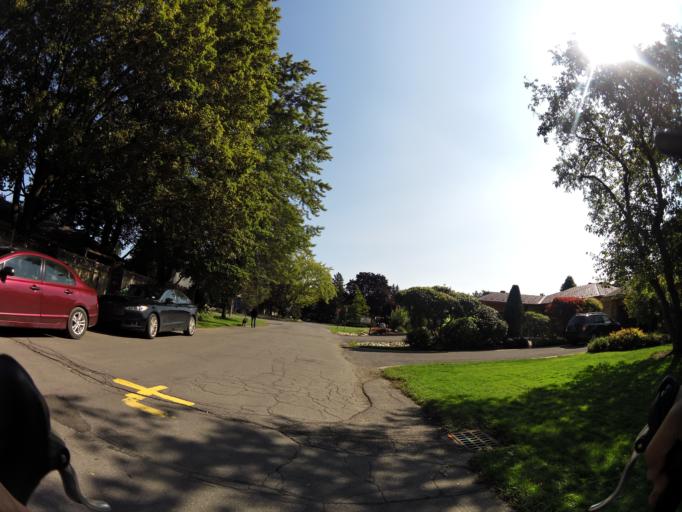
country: CA
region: Ontario
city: Ottawa
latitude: 45.3977
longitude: -75.6594
